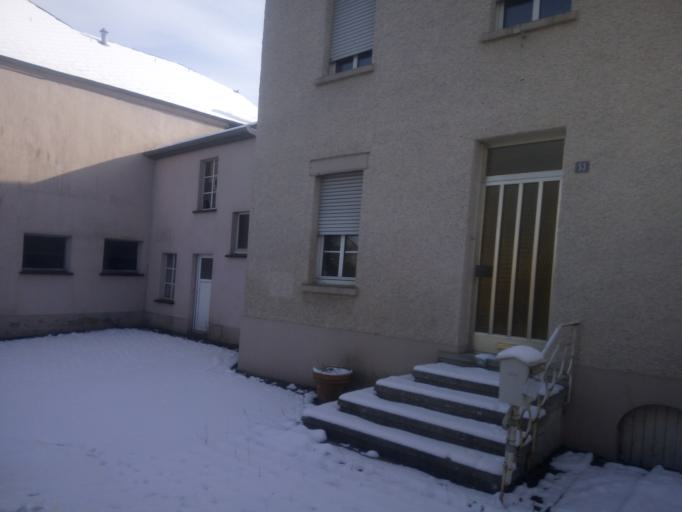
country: LU
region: Grevenmacher
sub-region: Canton d'Echternach
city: Consdorf
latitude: 49.7763
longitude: 6.3388
